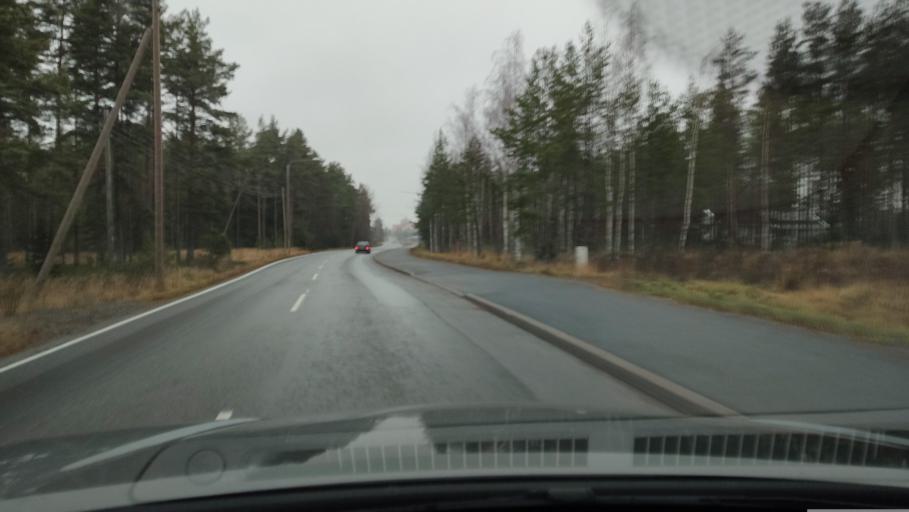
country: FI
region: Ostrobothnia
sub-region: Sydosterbotten
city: Kristinestad
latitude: 62.2355
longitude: 21.5209
